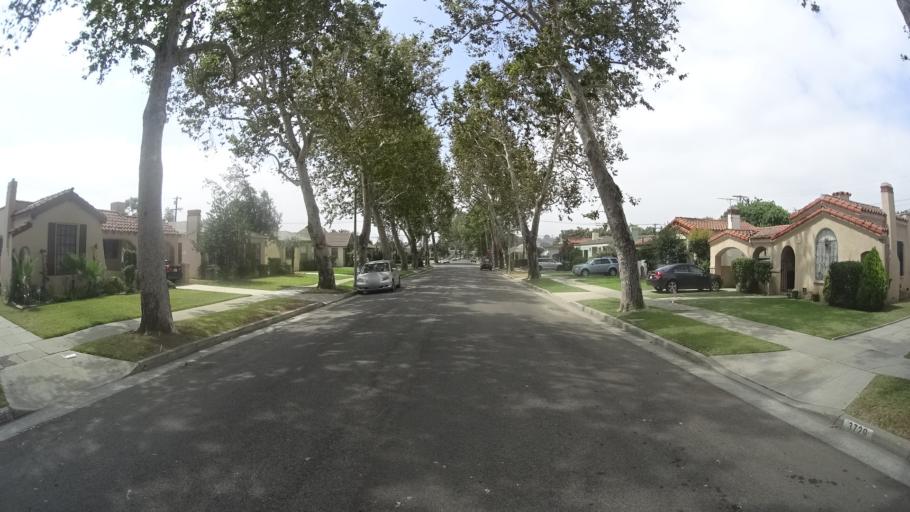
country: US
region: California
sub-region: Los Angeles County
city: View Park-Windsor Hills
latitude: 34.0192
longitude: -118.3383
